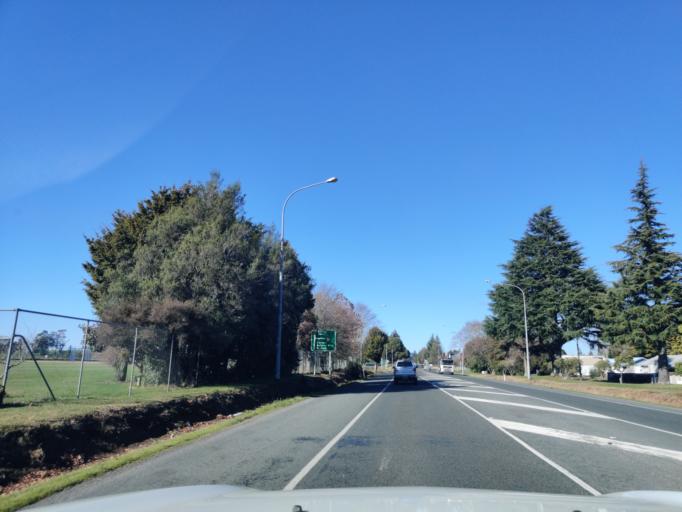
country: NZ
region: Waikato
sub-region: South Waikato District
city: Tokoroa
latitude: -38.2244
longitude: 175.8765
